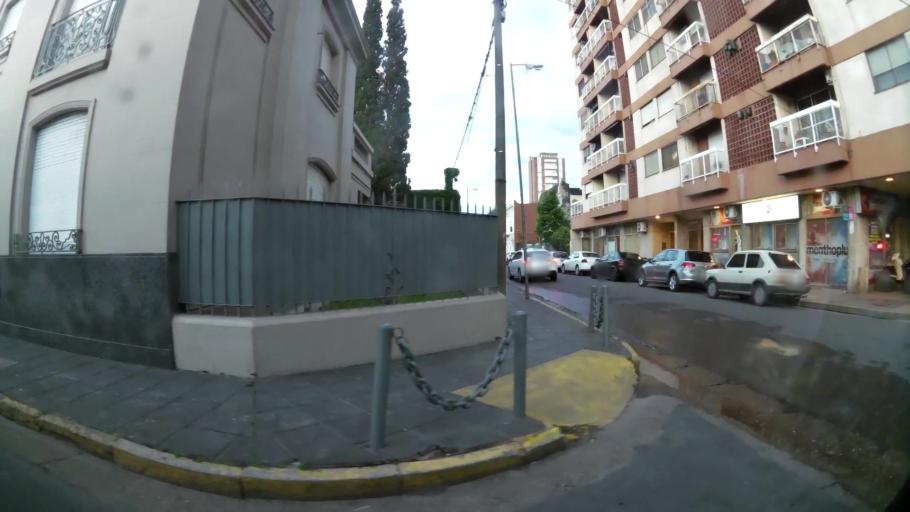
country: AR
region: Buenos Aires
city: San Nicolas de los Arroyos
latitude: -33.3301
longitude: -60.2146
